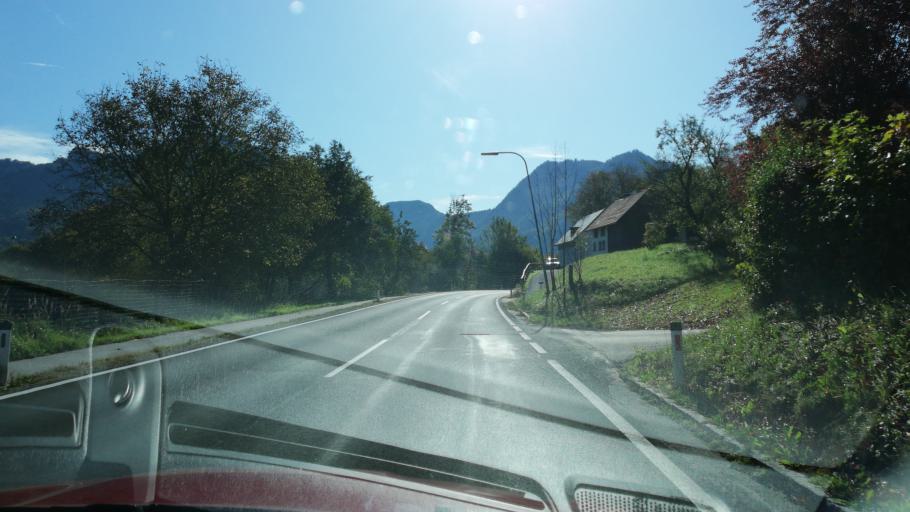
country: AT
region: Styria
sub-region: Politischer Bezirk Liezen
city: Landl
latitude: 47.6529
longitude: 14.7460
